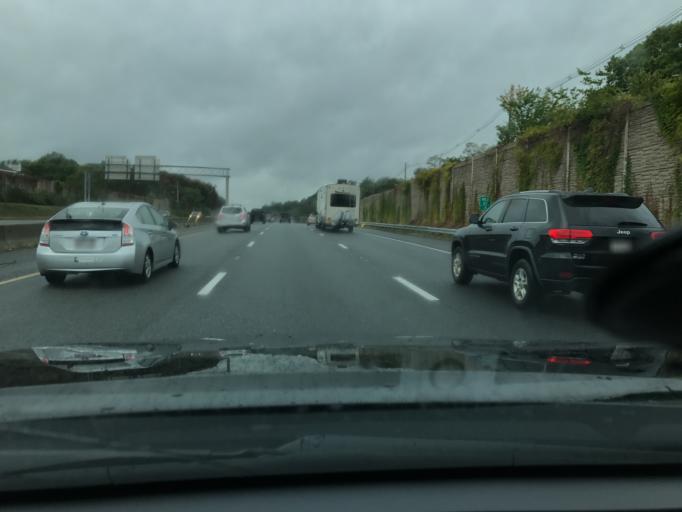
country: US
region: Massachusetts
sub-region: Essex County
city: Lynnfield
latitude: 42.5165
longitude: -71.0036
